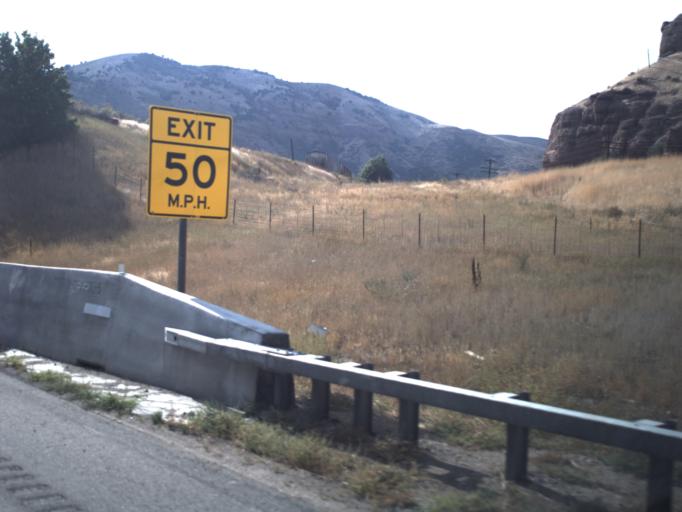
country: US
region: Utah
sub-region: Summit County
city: Coalville
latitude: 40.9722
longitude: -111.4370
